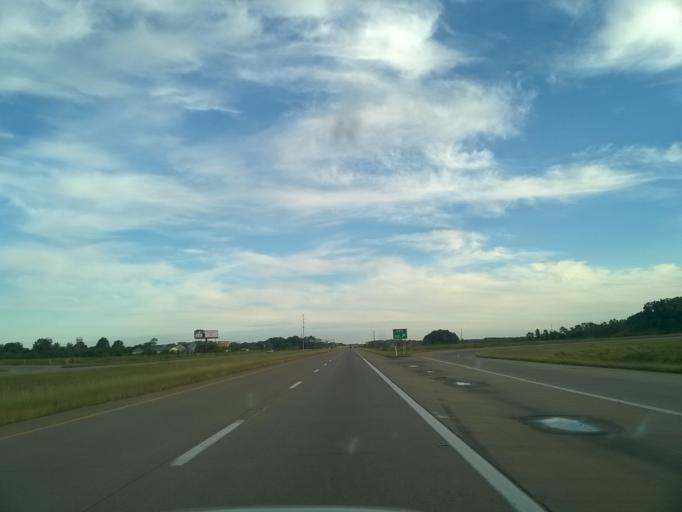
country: US
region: Indiana
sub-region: Vanderburgh County
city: Melody Hill
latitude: 38.0146
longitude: -87.4693
